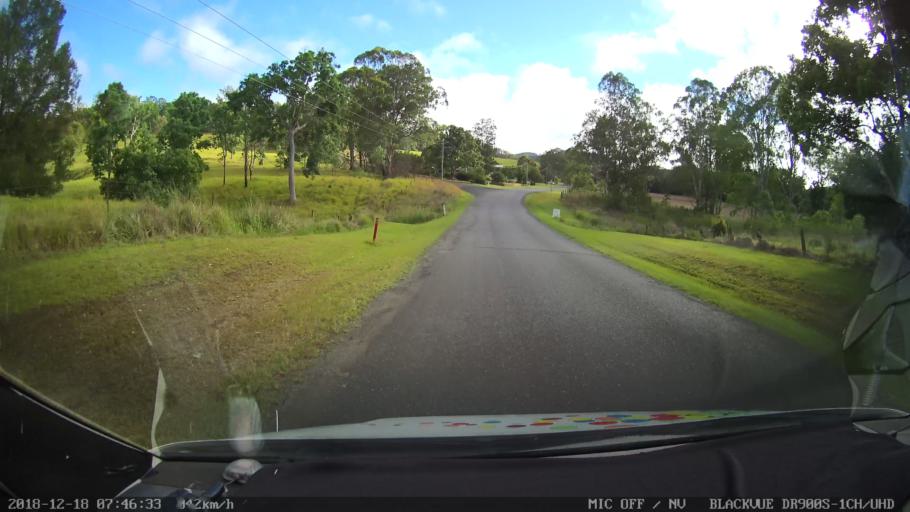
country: AU
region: New South Wales
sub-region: Kyogle
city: Kyogle
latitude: -28.4657
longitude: 152.5508
